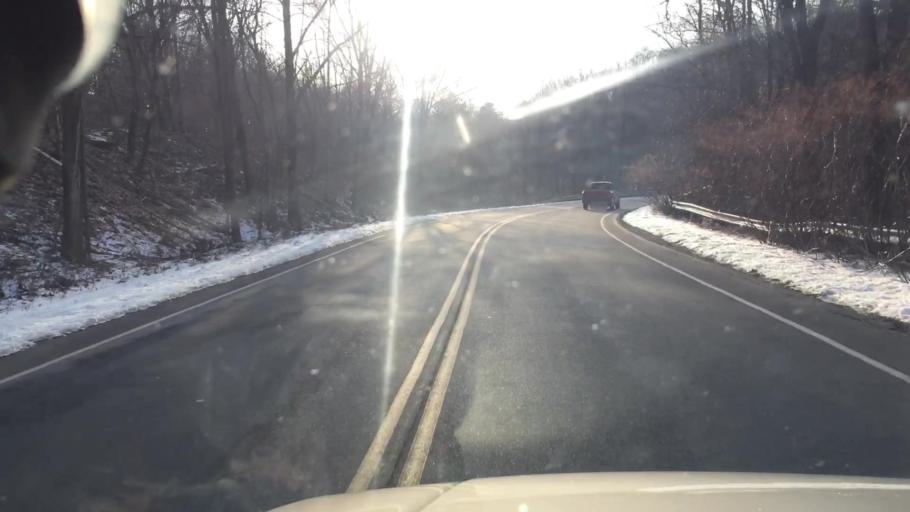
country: US
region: Pennsylvania
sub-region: Luzerne County
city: Nanticoke
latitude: 41.2066
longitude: -76.0084
